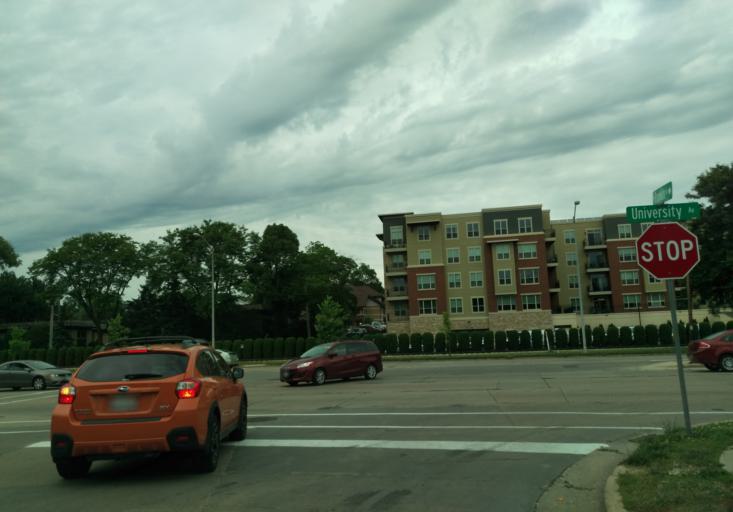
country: US
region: Wisconsin
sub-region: Dane County
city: Shorewood Hills
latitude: 43.0738
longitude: -89.4362
